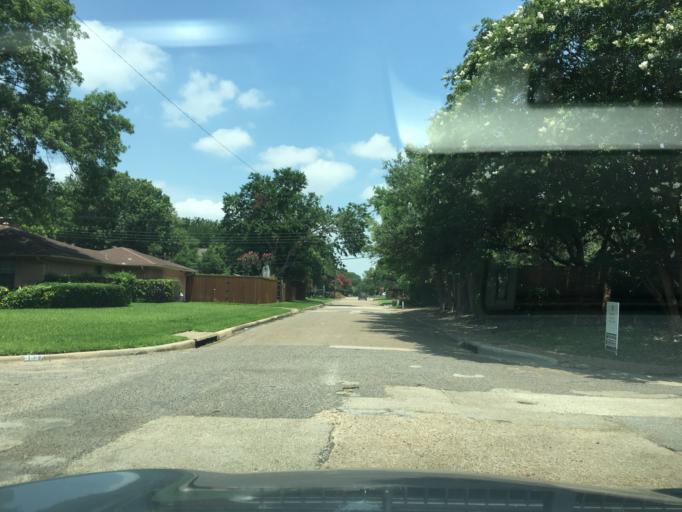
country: US
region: Texas
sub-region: Dallas County
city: Addison
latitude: 32.9119
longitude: -96.8074
